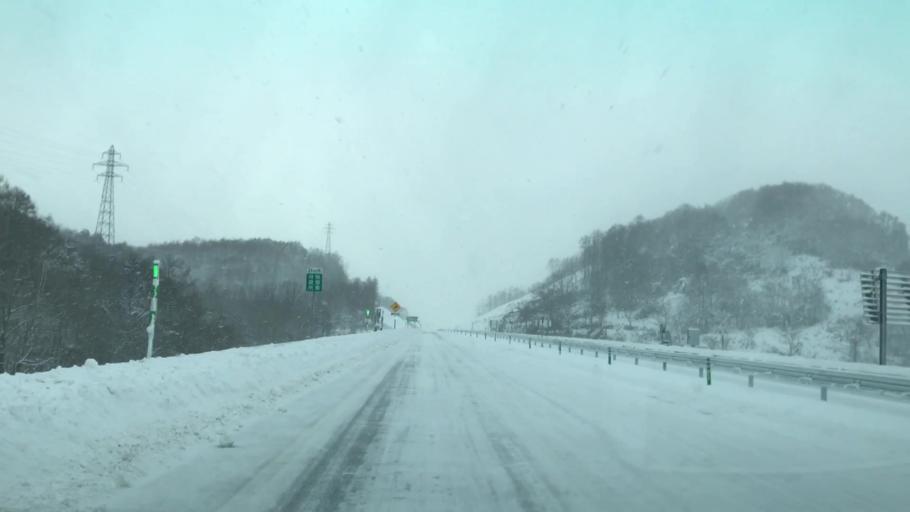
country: JP
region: Hokkaido
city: Otaru
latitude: 43.1975
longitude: 140.9179
